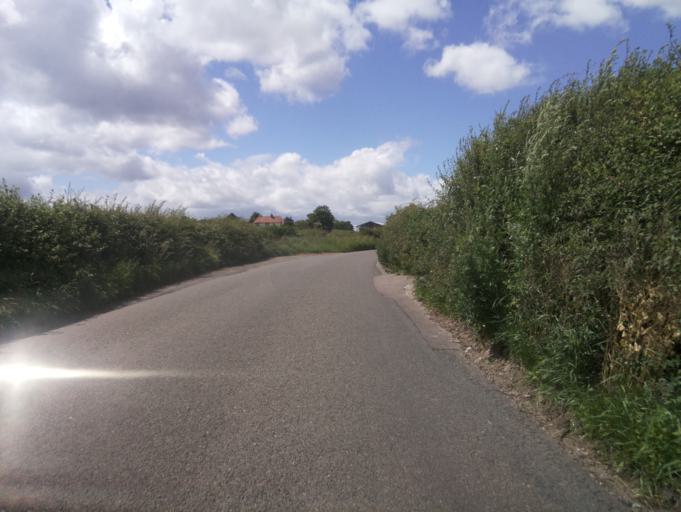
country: GB
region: England
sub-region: Nottinghamshire
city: Burton Joyce
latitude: 53.0035
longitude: -1.0715
